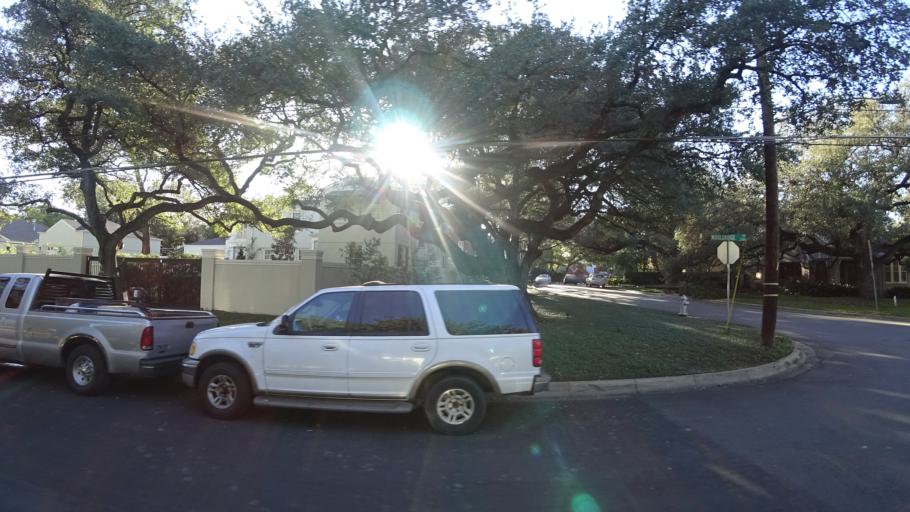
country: US
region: Texas
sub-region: Travis County
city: Austin
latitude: 30.2980
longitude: -97.7512
